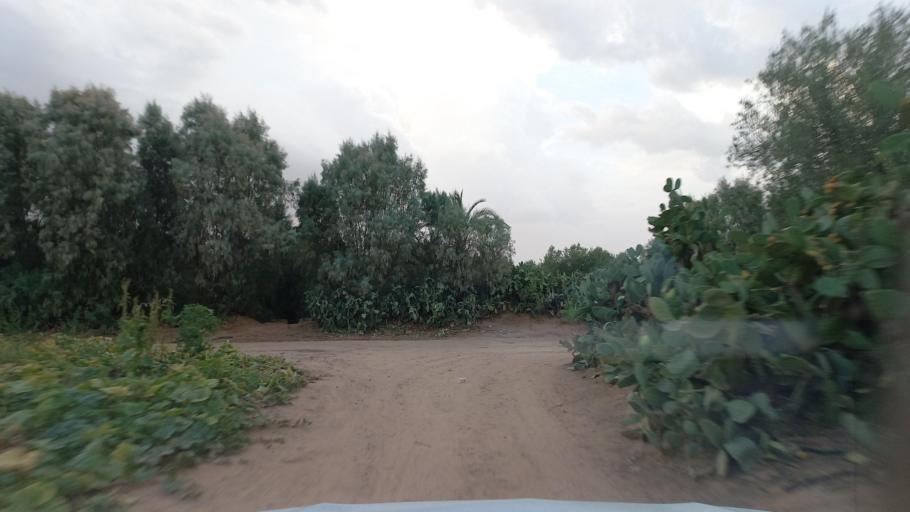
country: TN
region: Al Qasrayn
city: Kasserine
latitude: 35.2729
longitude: 9.0573
